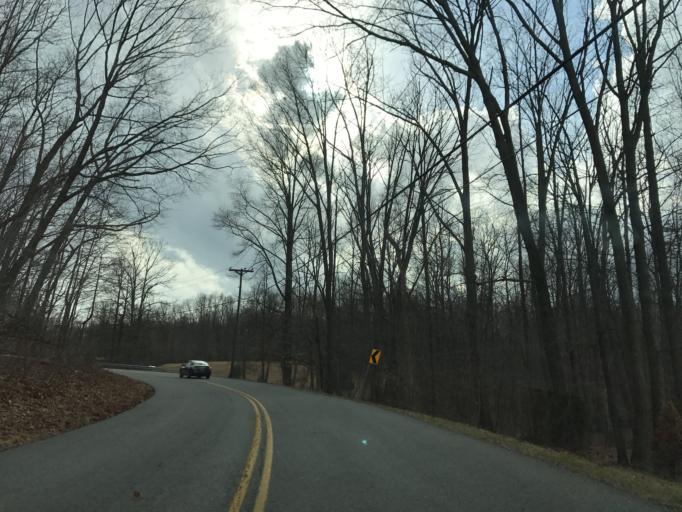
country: US
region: Maryland
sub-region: Harford County
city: South Bel Air
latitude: 39.5775
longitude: -76.3162
